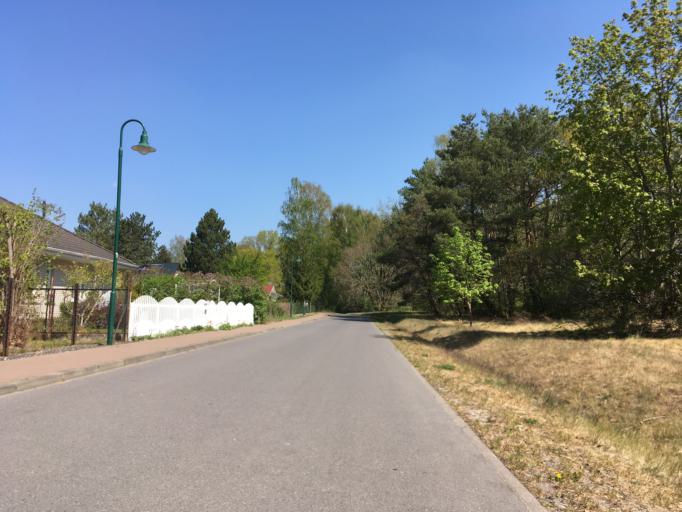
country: DE
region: Berlin
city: Buch
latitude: 52.6640
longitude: 13.5340
